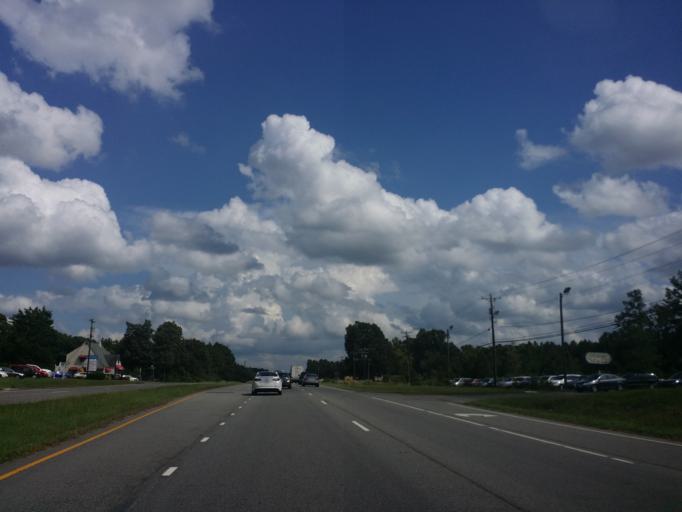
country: US
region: North Carolina
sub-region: Durham County
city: Durham
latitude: 35.9437
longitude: -78.8277
